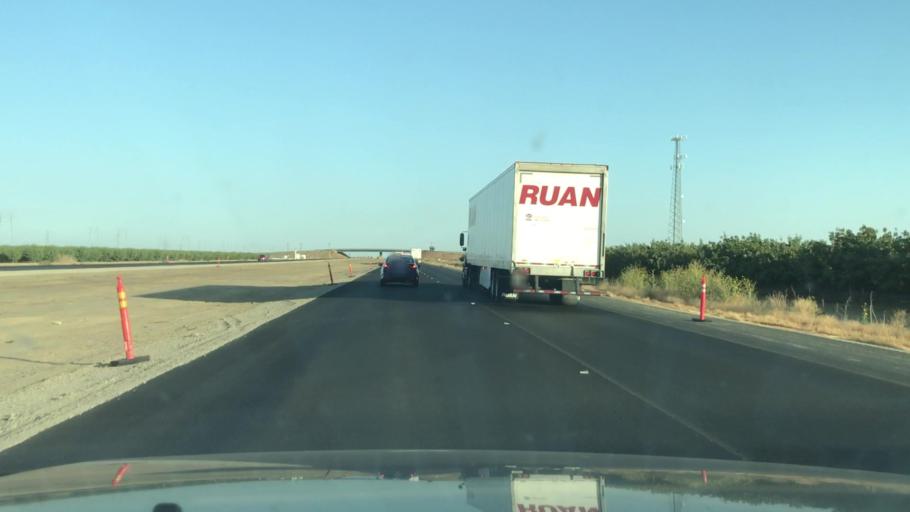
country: US
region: California
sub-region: Kings County
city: Kettleman City
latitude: 35.8801
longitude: -119.8572
